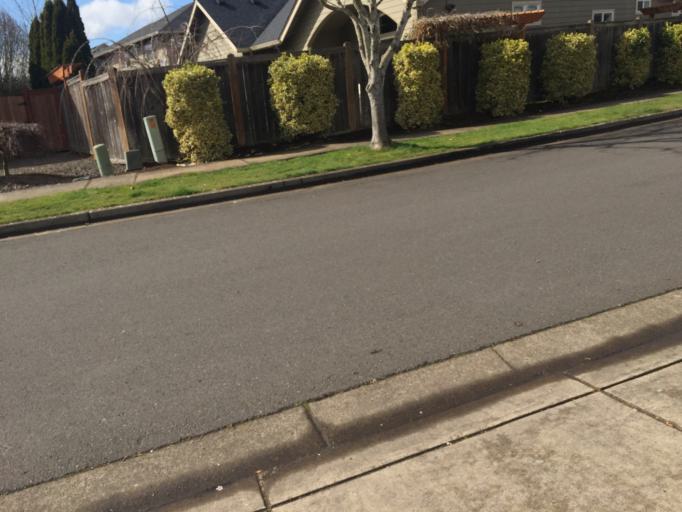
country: US
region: Oregon
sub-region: Lane County
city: Eugene
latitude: 44.1024
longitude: -123.1549
